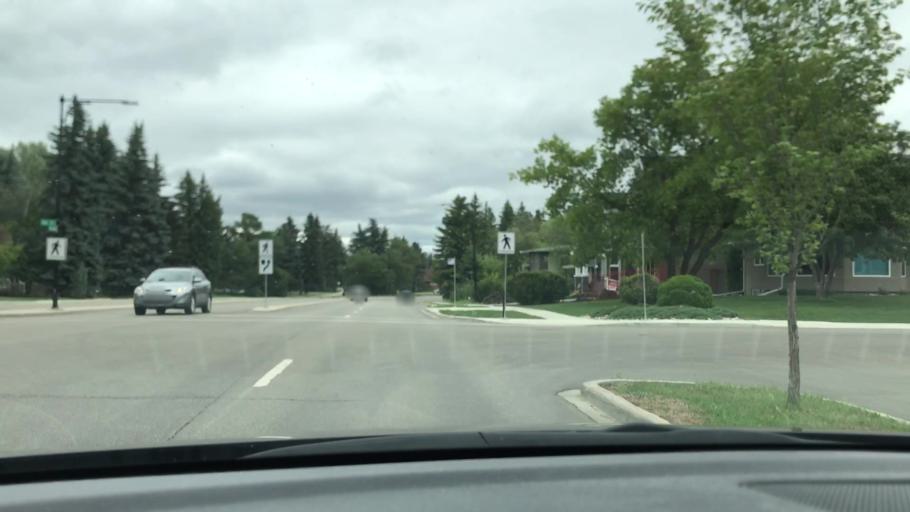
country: CA
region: Alberta
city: Edmonton
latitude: 53.5193
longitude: -113.5630
